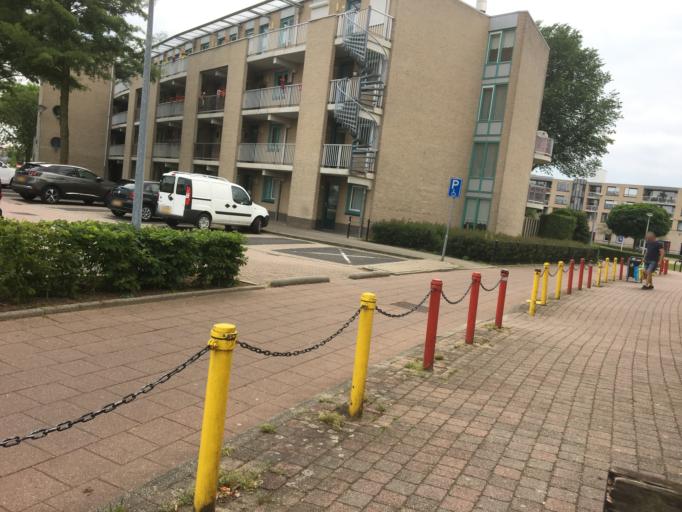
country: NL
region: Gelderland
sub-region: Gemeente Duiven
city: Duiven
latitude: 51.9416
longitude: 6.0081
